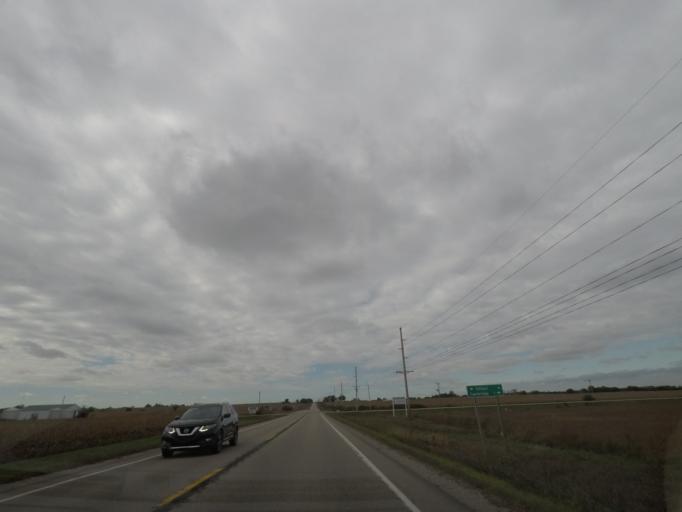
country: US
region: Iowa
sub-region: Story County
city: Huxley
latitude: 41.8778
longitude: -93.5298
